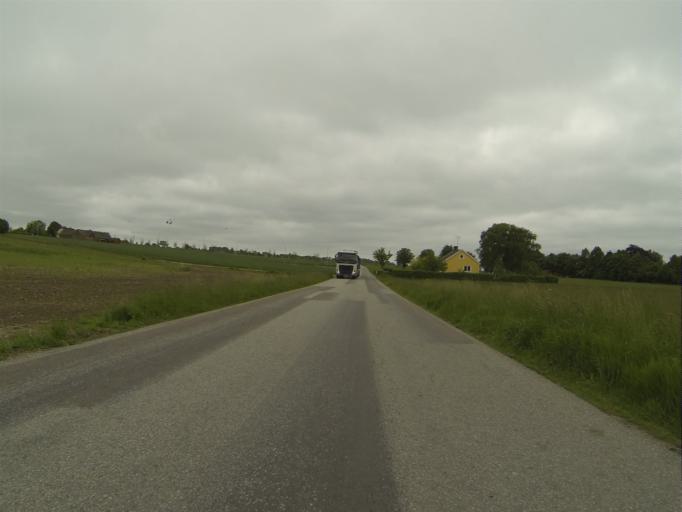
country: SE
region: Skane
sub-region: Lunds Kommun
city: Genarp
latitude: 55.6585
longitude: 13.3475
